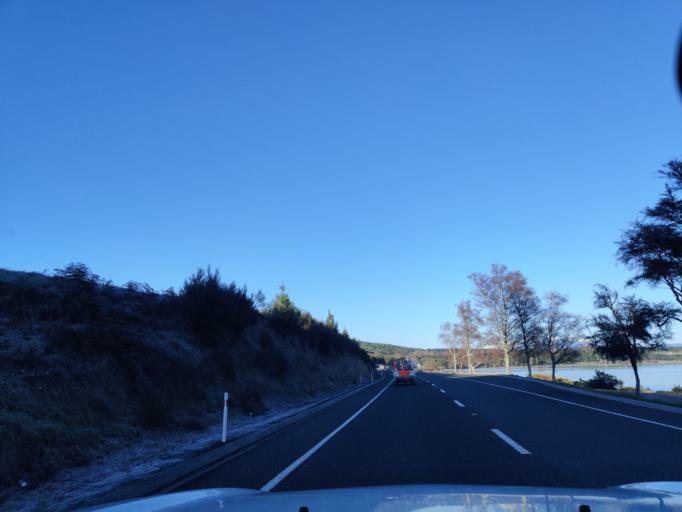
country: NZ
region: Waikato
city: Turangi
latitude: -38.8973
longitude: 175.9462
